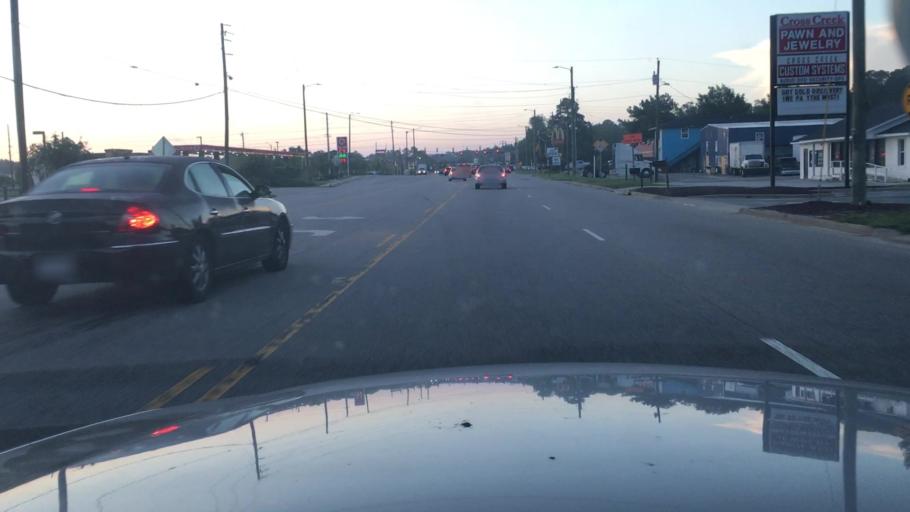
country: US
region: North Carolina
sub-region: Cumberland County
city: Fort Bragg
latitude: 35.0624
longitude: -79.0177
